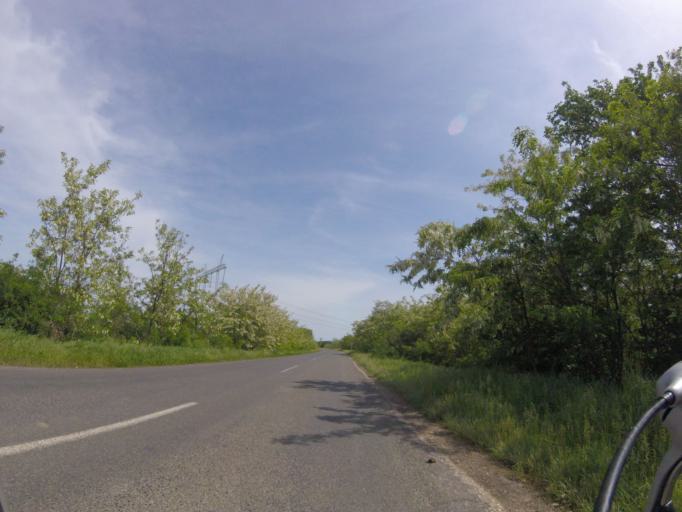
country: HU
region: Jasz-Nagykun-Szolnok
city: Tiszabo
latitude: 47.2878
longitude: 20.3897
